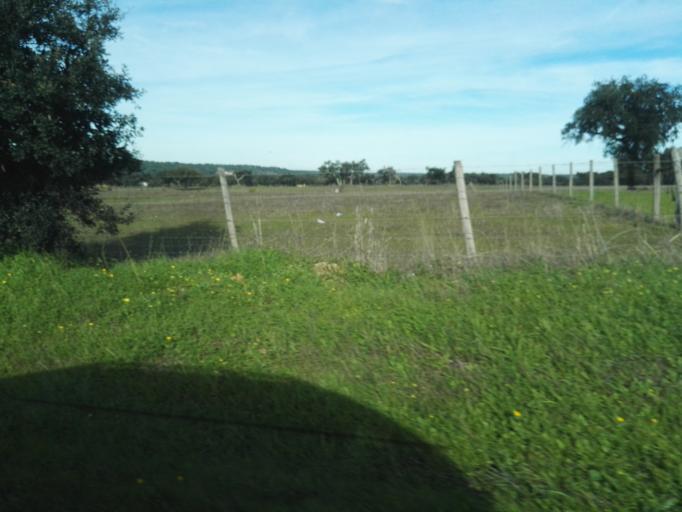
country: PT
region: Evora
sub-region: Mora
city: Mora
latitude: 38.9446
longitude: -8.1411
